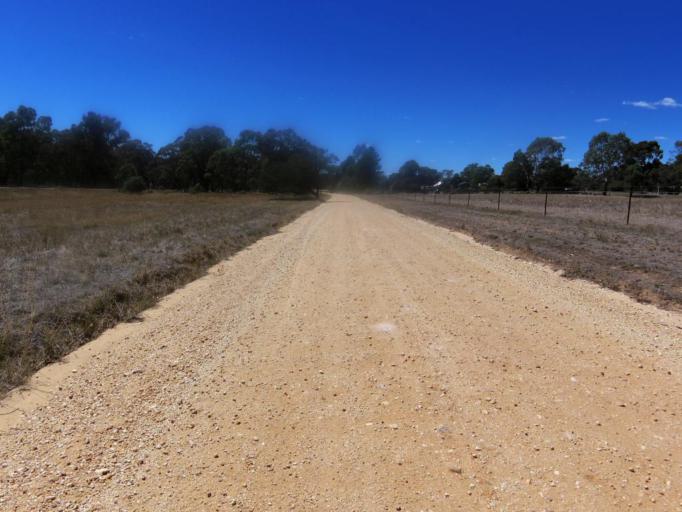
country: AU
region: Victoria
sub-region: Mount Alexander
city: Castlemaine
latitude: -36.9928
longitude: 144.0792
